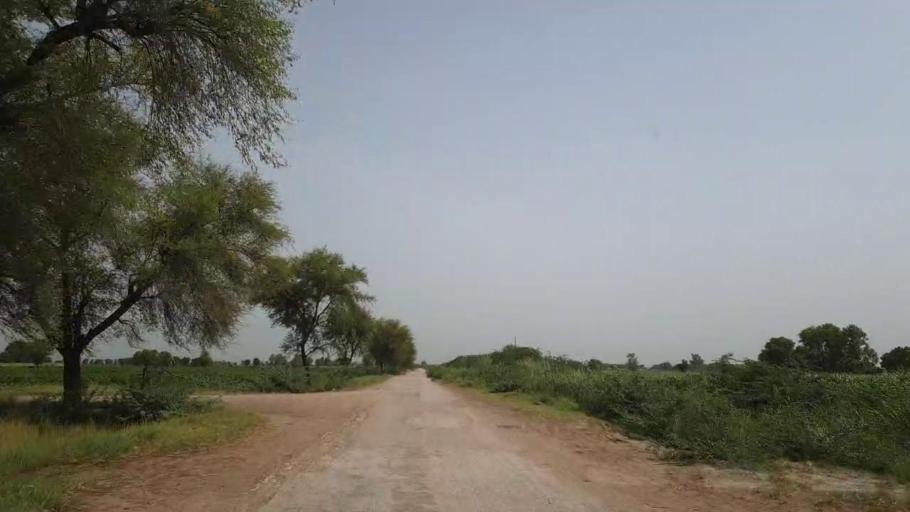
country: PK
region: Sindh
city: Sakrand
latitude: 26.1347
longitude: 68.3642
